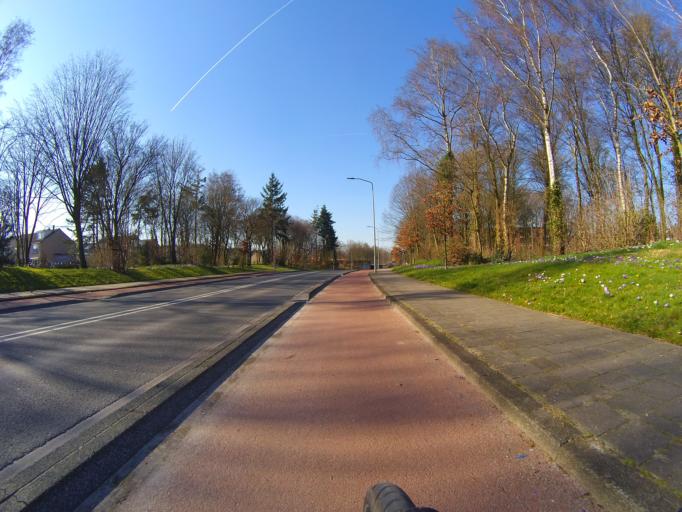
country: NL
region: Gelderland
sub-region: Gemeente Nijkerk
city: Nijkerk
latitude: 52.2181
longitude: 5.4916
